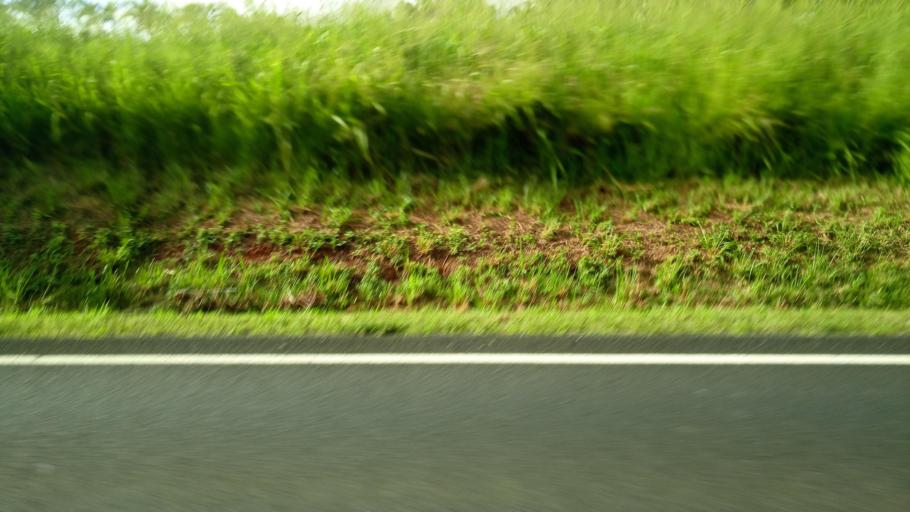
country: AU
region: Queensland
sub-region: Cassowary Coast
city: Innisfail
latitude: -17.5579
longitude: 145.9561
